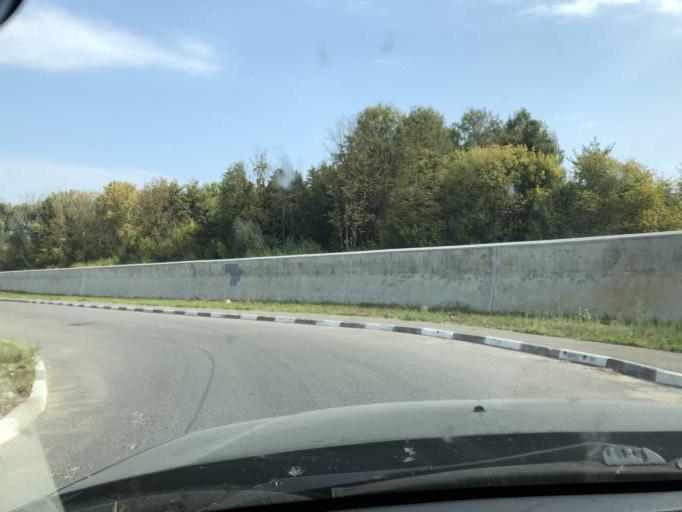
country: RU
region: Tula
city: Tula
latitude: 54.1916
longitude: 37.6423
